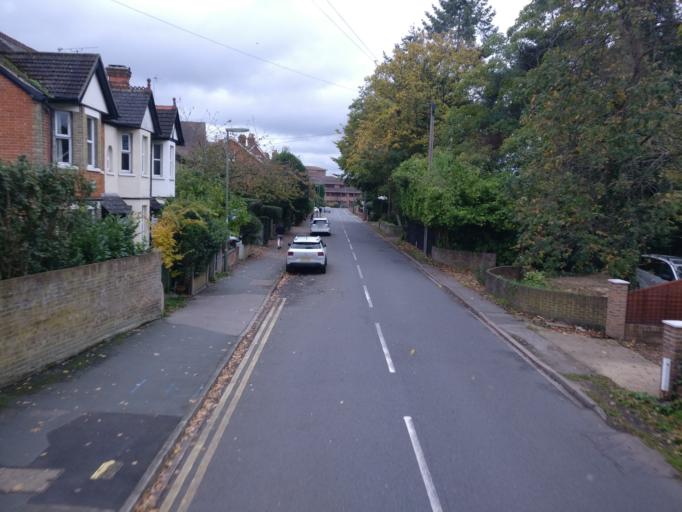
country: GB
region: England
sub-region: Surrey
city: Camberley
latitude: 51.3419
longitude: -0.7445
